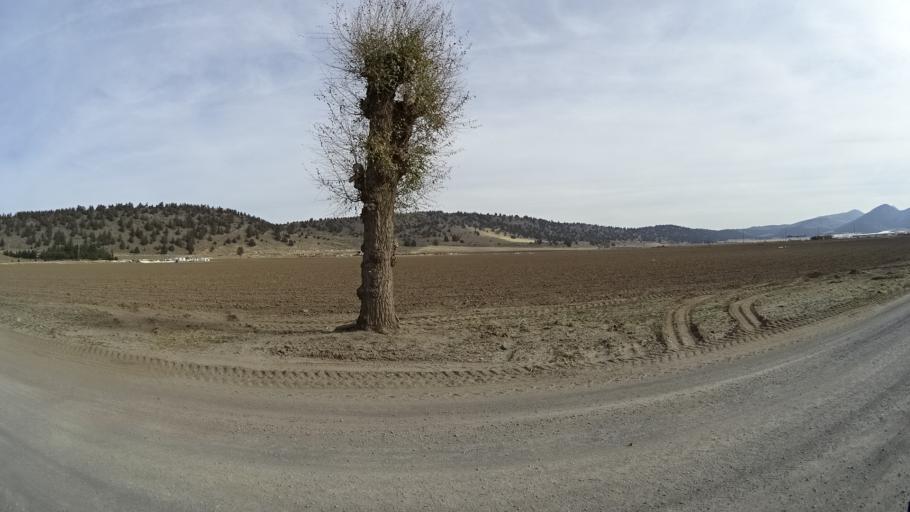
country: US
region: Oregon
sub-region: Klamath County
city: Klamath Falls
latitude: 41.9642
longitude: -121.9114
